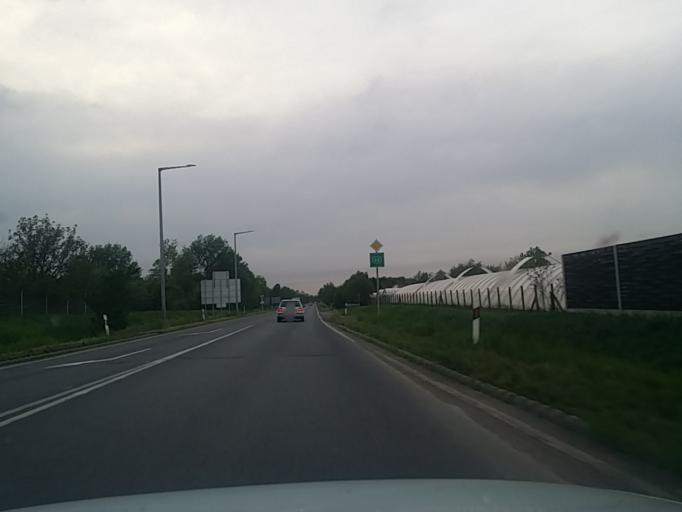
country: HU
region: Bekes
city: Gyula
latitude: 46.6338
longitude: 21.2575
